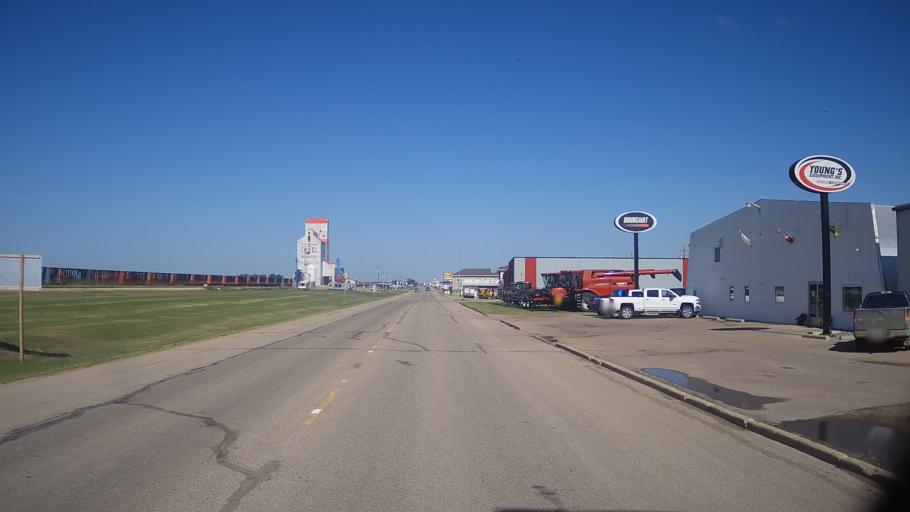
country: CA
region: Saskatchewan
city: Watrous
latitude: 51.6667
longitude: -105.4540
